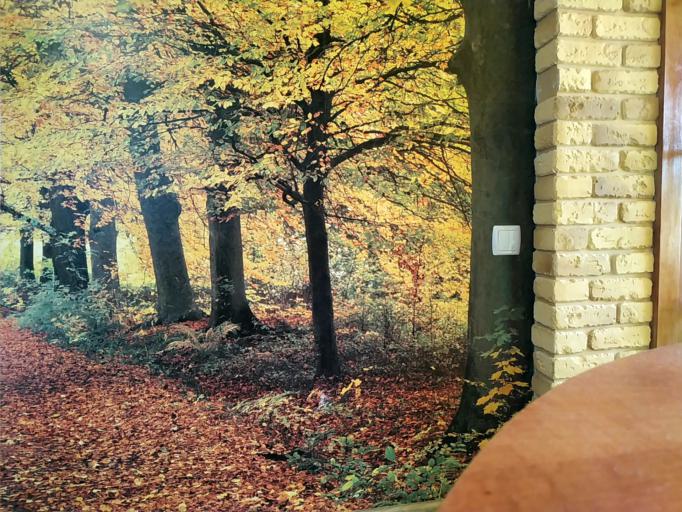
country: RU
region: Novgorod
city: Sol'tsy
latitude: 57.9057
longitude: 30.2133
